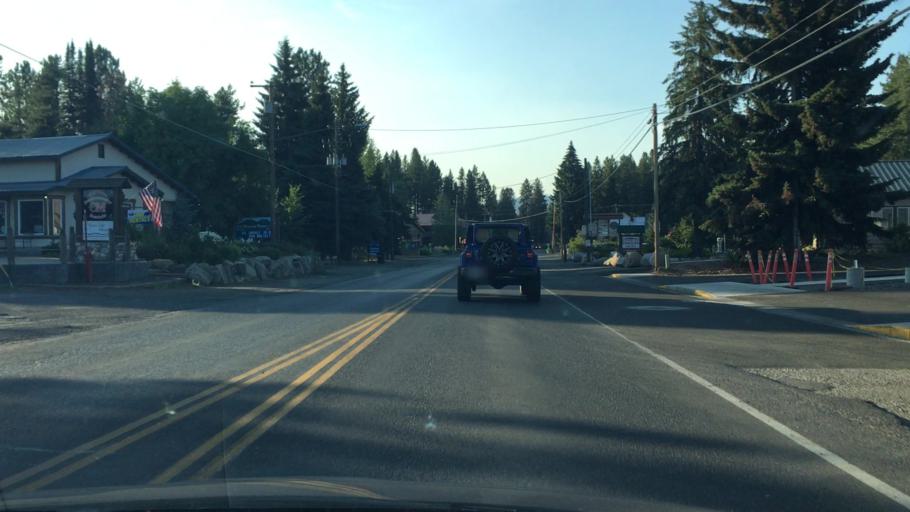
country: US
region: Idaho
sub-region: Valley County
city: McCall
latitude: 44.8992
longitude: -116.0972
